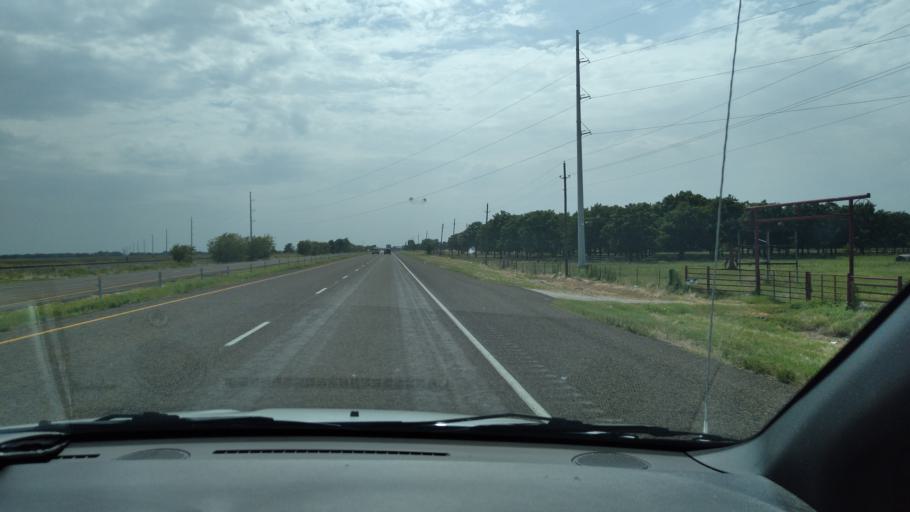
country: US
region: Texas
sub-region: Navarro County
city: Kerens
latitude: 32.1212
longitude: -96.3030
